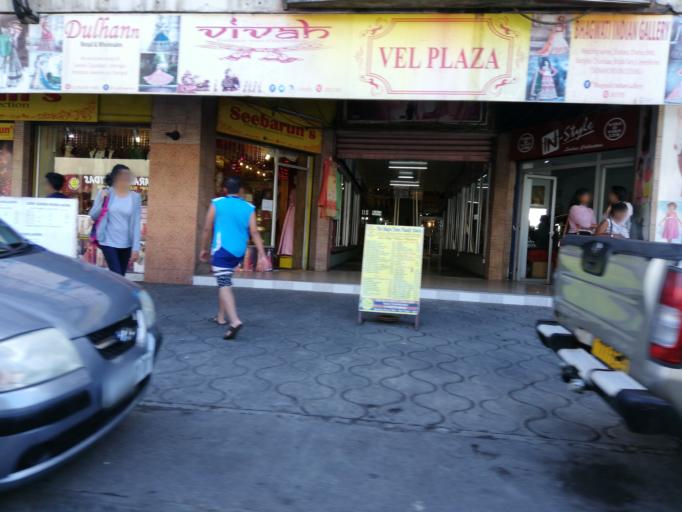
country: MU
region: Riviere du Rempart
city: Goodlands
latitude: -20.0371
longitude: 57.6495
